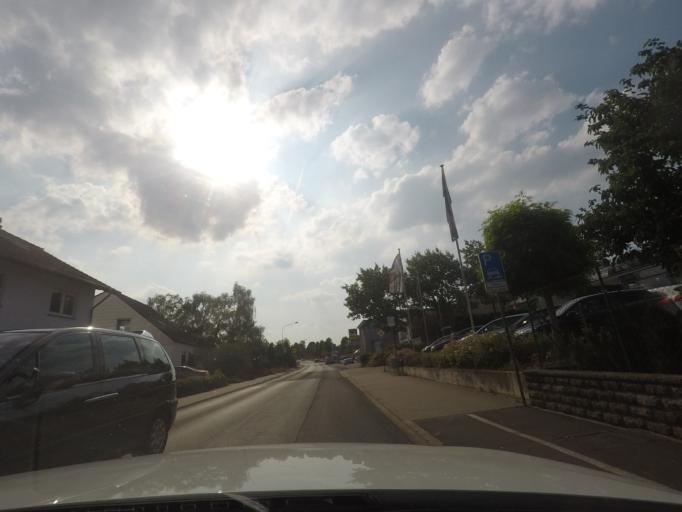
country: DE
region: Rheinland-Pfalz
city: Meddersheim
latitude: 49.7875
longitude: 7.6408
